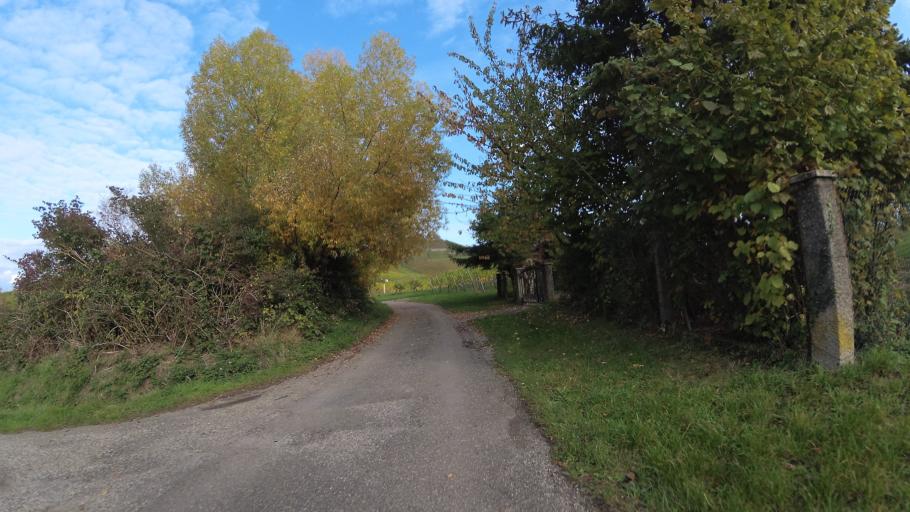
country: DE
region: Baden-Wuerttemberg
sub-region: Regierungsbezirk Stuttgart
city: Neckarsulm
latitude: 49.1944
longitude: 9.2428
